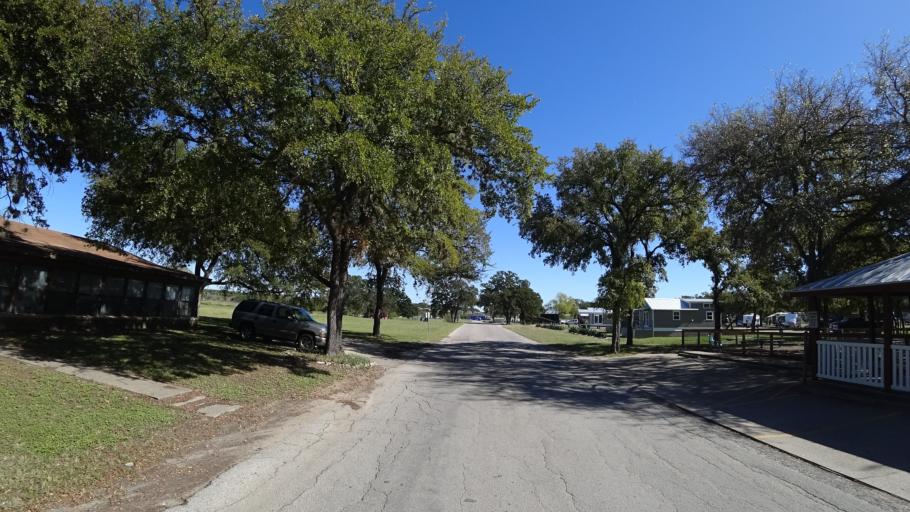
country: US
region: Texas
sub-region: Travis County
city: Hornsby Bend
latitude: 30.2850
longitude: -97.6360
